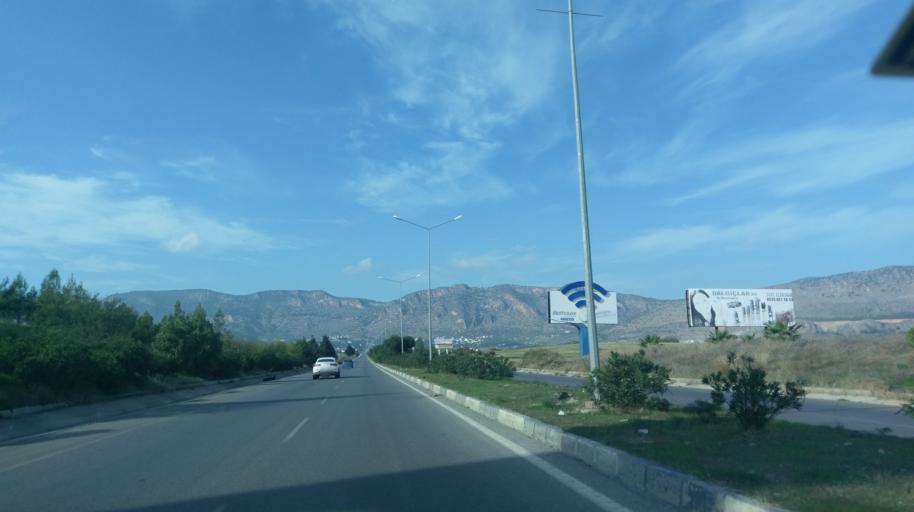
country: CY
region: Keryneia
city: Kyrenia
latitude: 35.2621
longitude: 33.2957
